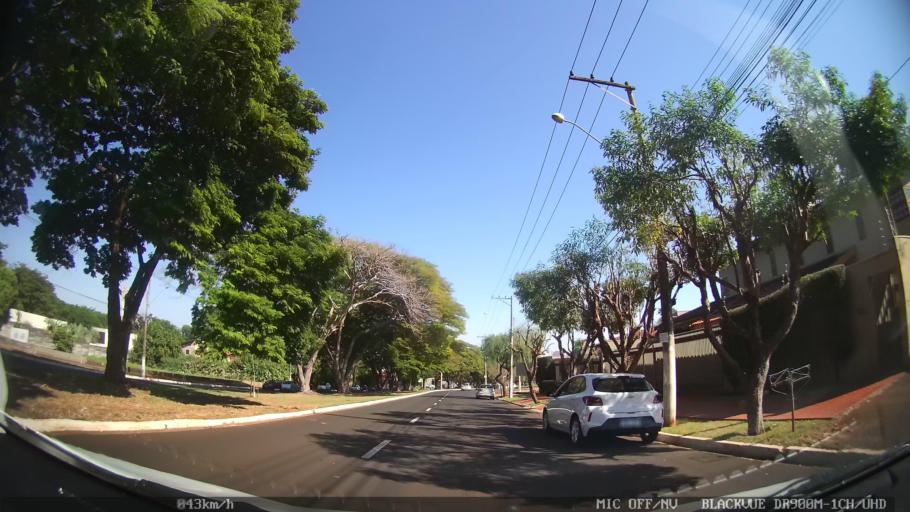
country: BR
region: Sao Paulo
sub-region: Ribeirao Preto
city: Ribeirao Preto
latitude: -21.2198
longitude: -47.8094
